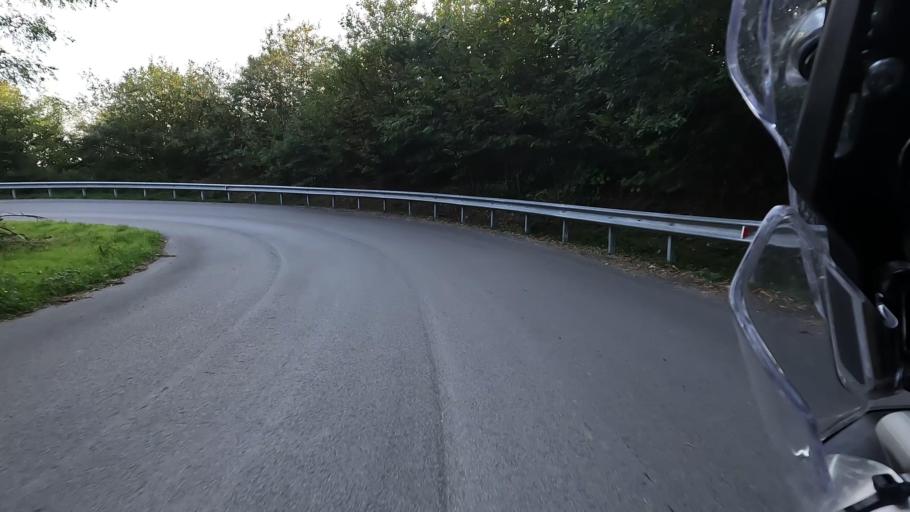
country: IT
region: Liguria
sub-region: Provincia di Savona
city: San Giovanni
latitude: 44.4131
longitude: 8.5193
